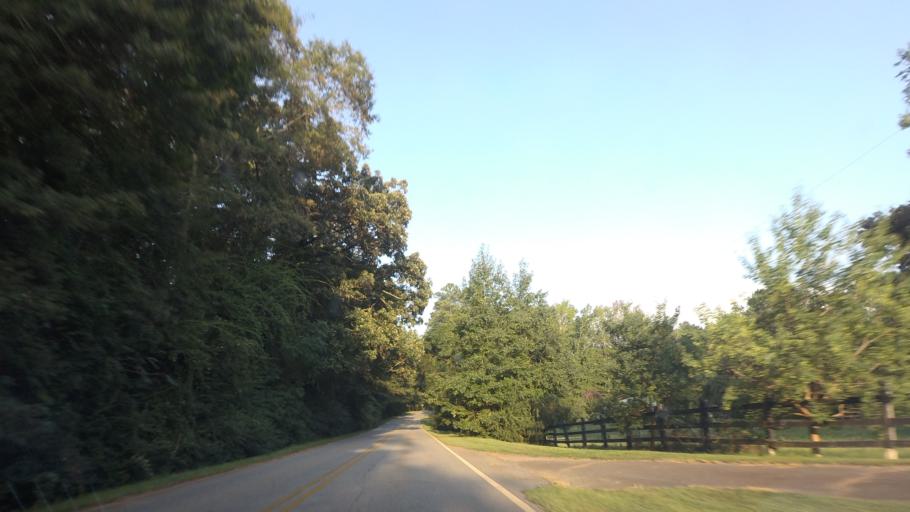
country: US
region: Georgia
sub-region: Bibb County
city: West Point
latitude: 32.8970
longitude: -83.8047
